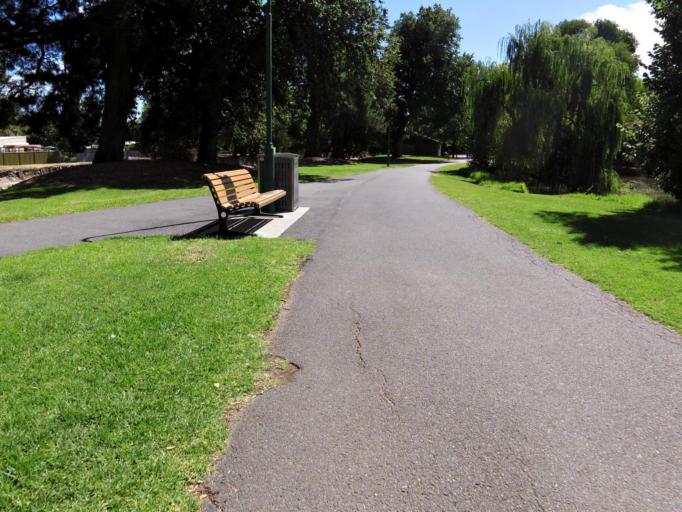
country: AU
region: Victoria
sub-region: Greater Bendigo
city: Bendigo
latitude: -36.7479
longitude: 144.2896
